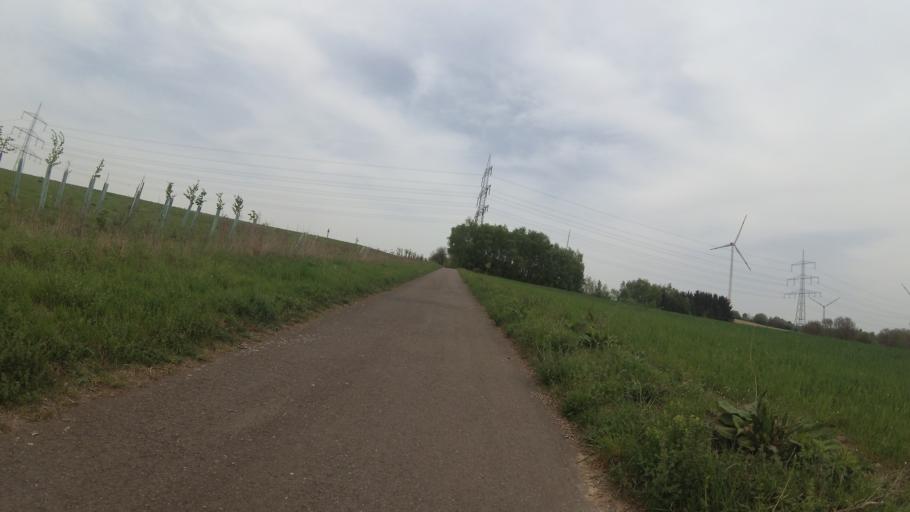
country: DE
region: Saarland
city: Schiffweiler
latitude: 49.3798
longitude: 7.1376
